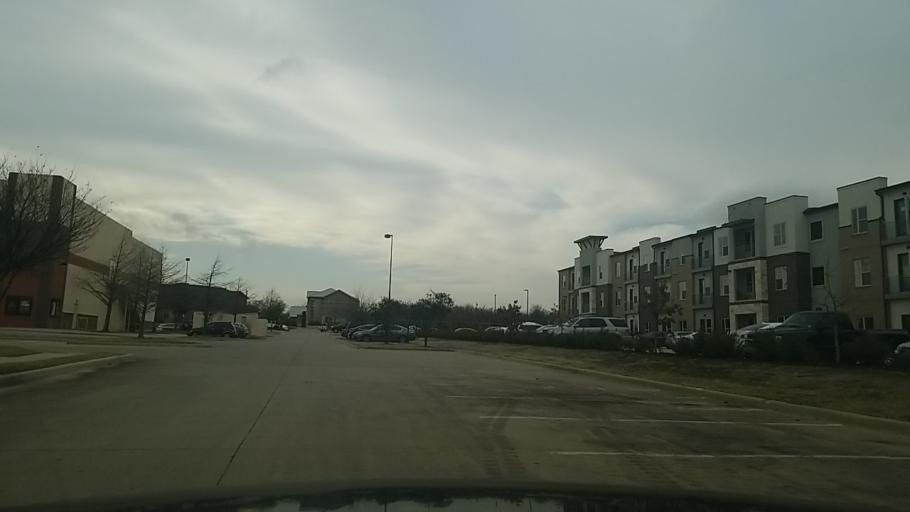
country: US
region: Texas
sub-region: Denton County
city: Corinth
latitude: 33.1768
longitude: -97.0984
